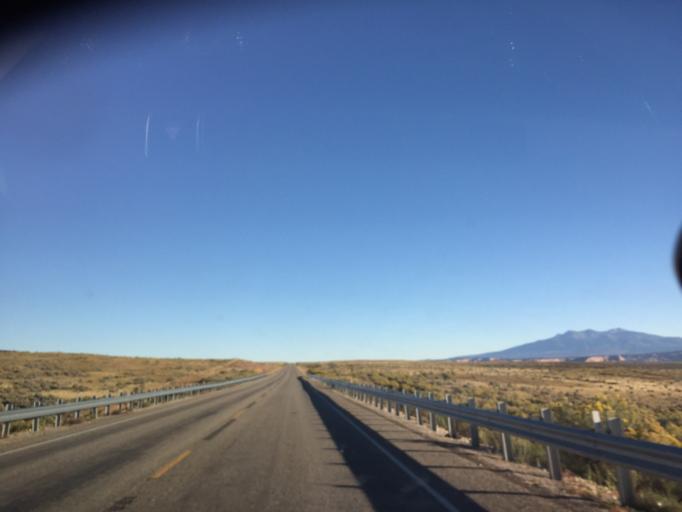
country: US
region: Utah
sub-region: San Juan County
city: Monticello
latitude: 38.1163
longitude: -109.3655
